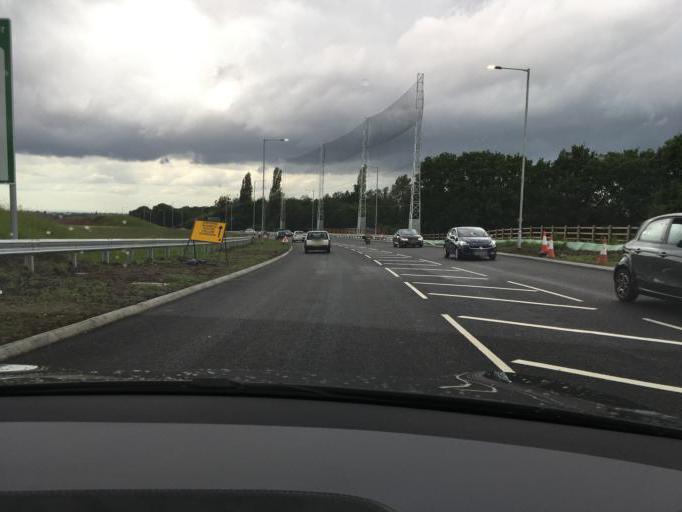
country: GB
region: England
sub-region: Borough of Stockport
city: Hazel Grove
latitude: 53.3686
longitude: -2.0948
